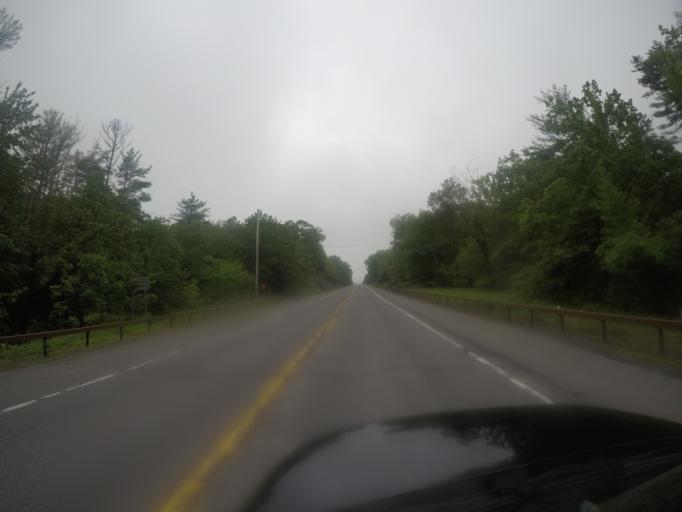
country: US
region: New York
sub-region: Ulster County
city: West Hurley
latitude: 41.9984
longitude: -74.1114
